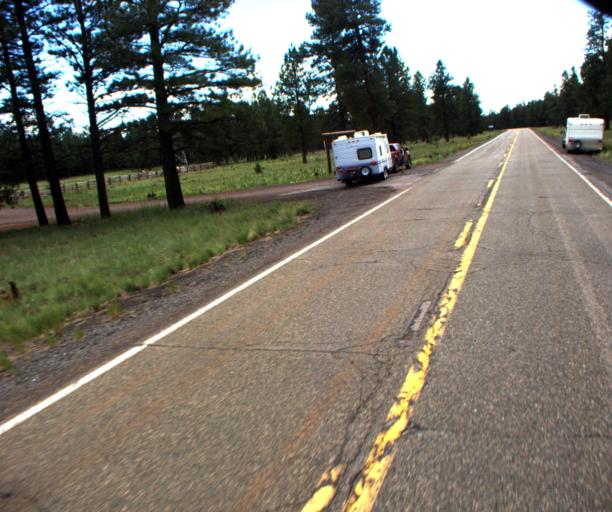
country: US
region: Arizona
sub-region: Coconino County
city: Parks
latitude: 35.3670
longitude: -111.7910
